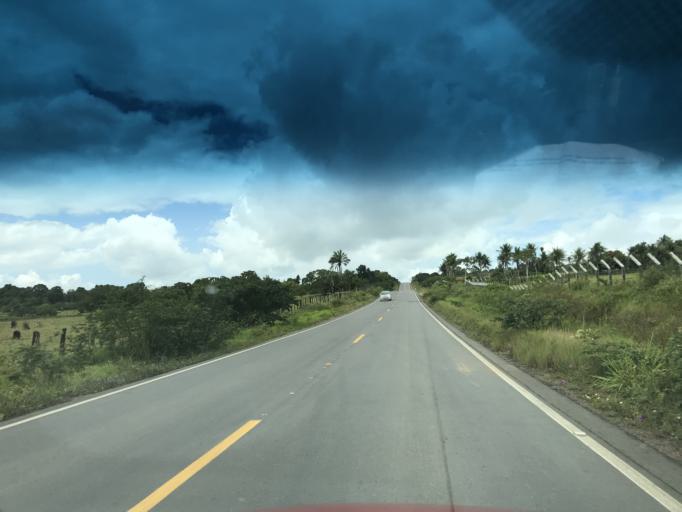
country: BR
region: Bahia
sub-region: Conceicao Do Almeida
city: Conceicao do Almeida
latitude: -12.6887
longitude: -39.2491
